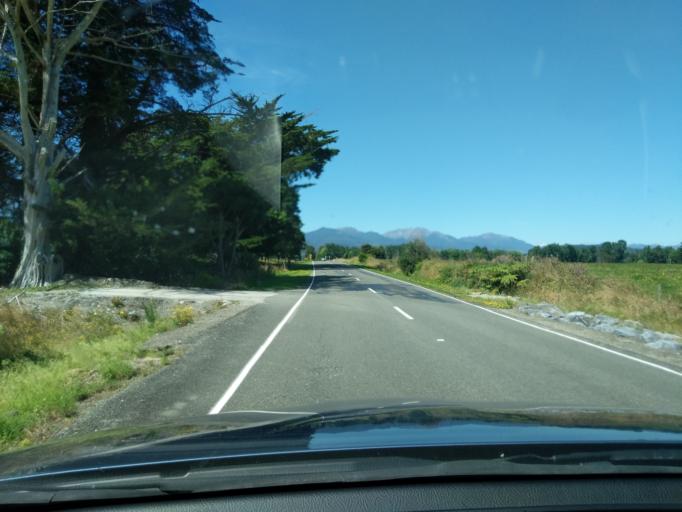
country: NZ
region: Tasman
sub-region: Tasman District
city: Takaka
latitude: -40.6986
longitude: 172.6325
